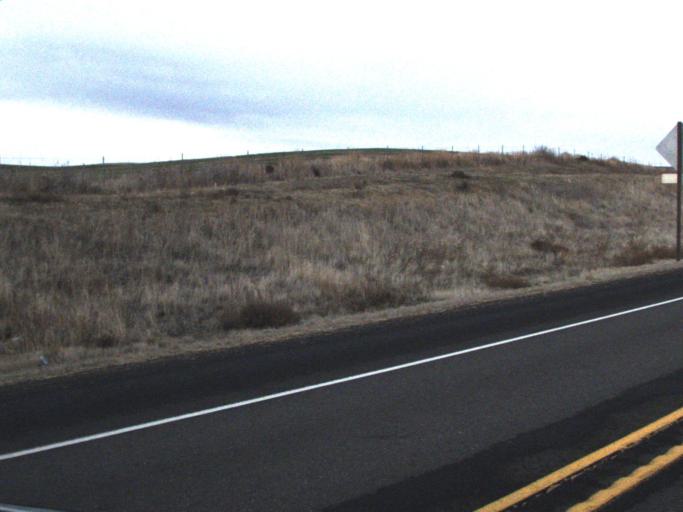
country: US
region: Washington
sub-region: Walla Walla County
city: Garrett
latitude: 46.0503
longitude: -118.5170
